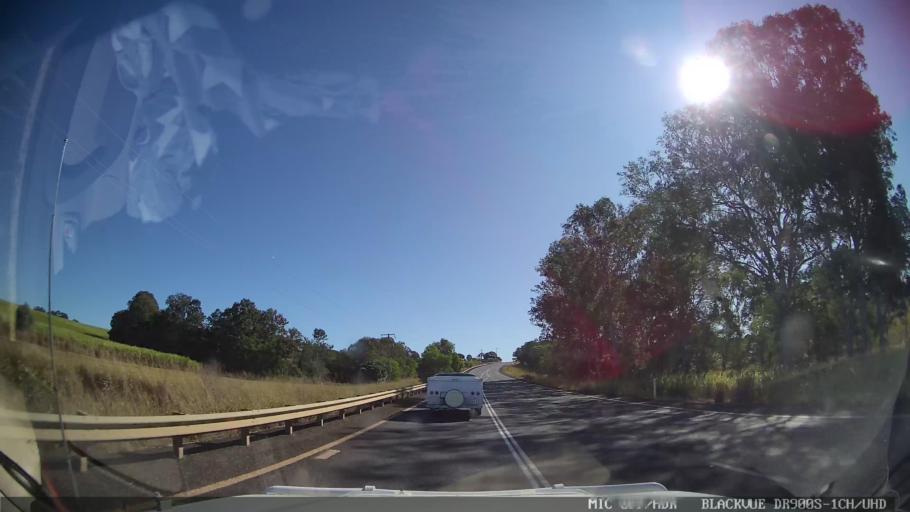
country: AU
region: Queensland
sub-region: Bundaberg
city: Childers
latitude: -25.2468
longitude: 152.3189
